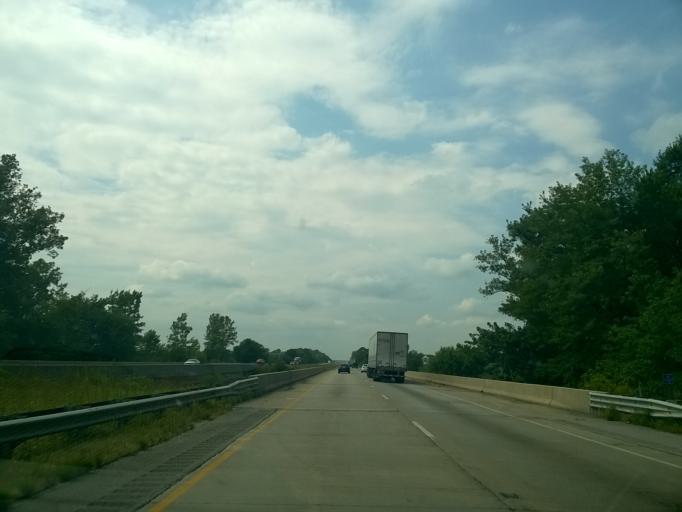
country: US
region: Indiana
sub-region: Putnam County
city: Cloverdale
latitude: 39.5608
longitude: -86.6558
